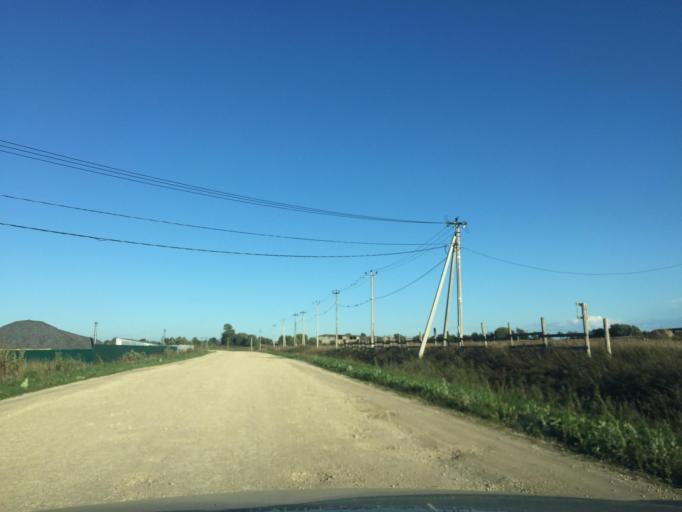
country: RU
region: Leningrad
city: Siverskiy
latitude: 59.3305
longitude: 30.0202
